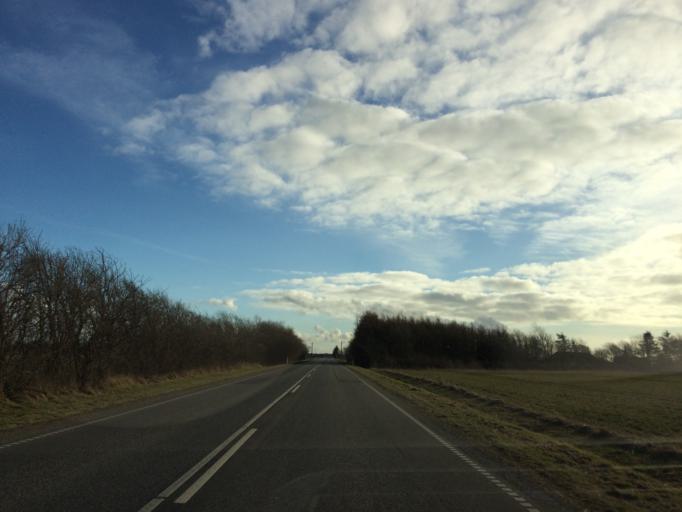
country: DK
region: Central Jutland
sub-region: Lemvig Kommune
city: Lemvig
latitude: 56.4500
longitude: 8.2944
